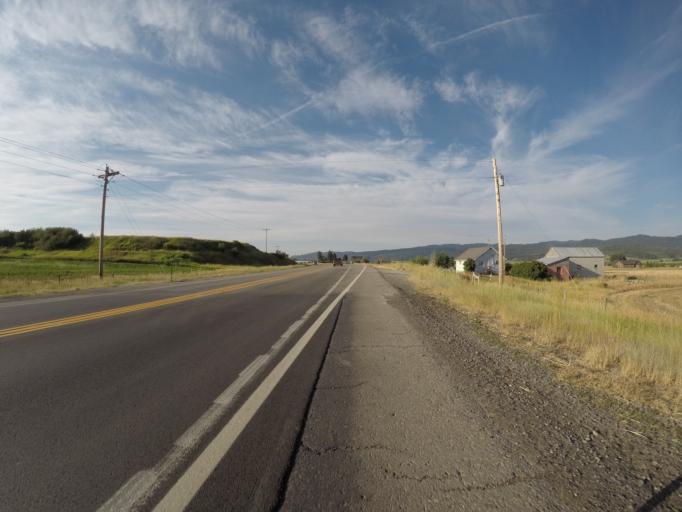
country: US
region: Wyoming
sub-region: Lincoln County
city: Afton
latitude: 42.9550
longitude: -111.0127
